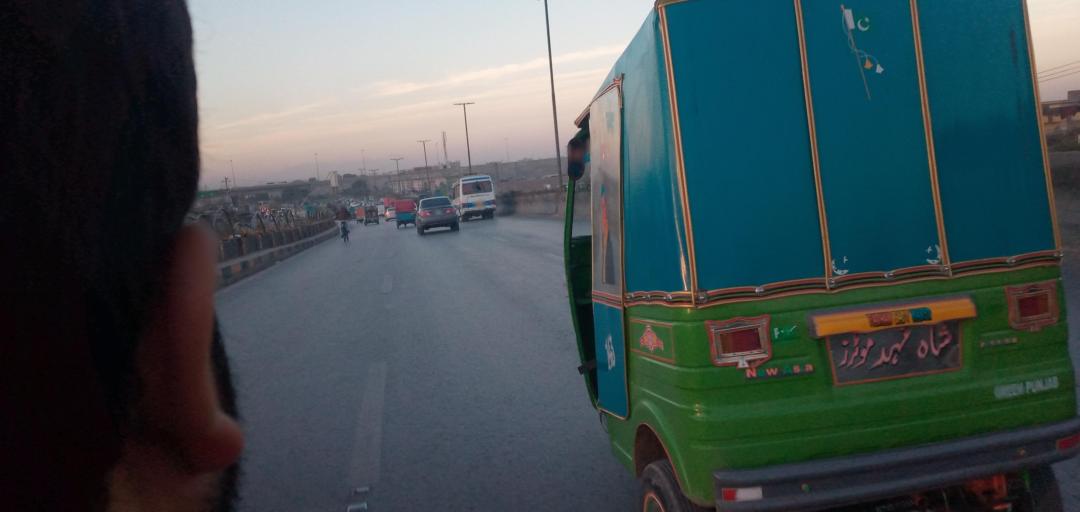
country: PK
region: Khyber Pakhtunkhwa
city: Peshawar
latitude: 34.0201
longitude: 71.6217
